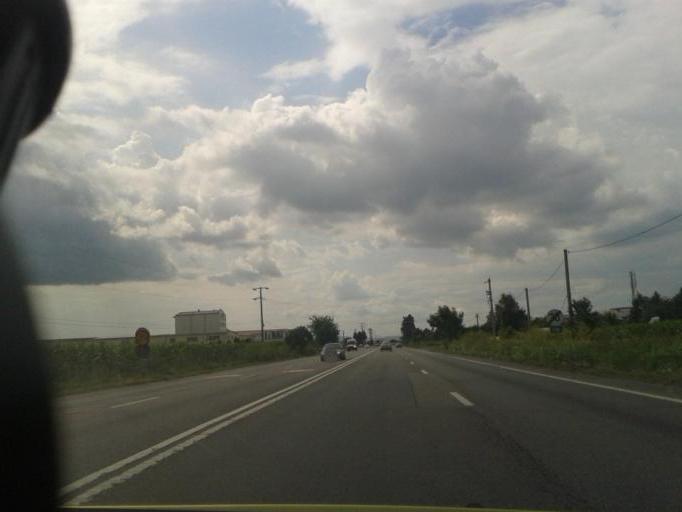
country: RO
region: Prahova
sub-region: Comuna Paulesti
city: Gageni
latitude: 44.9857
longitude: 25.9230
